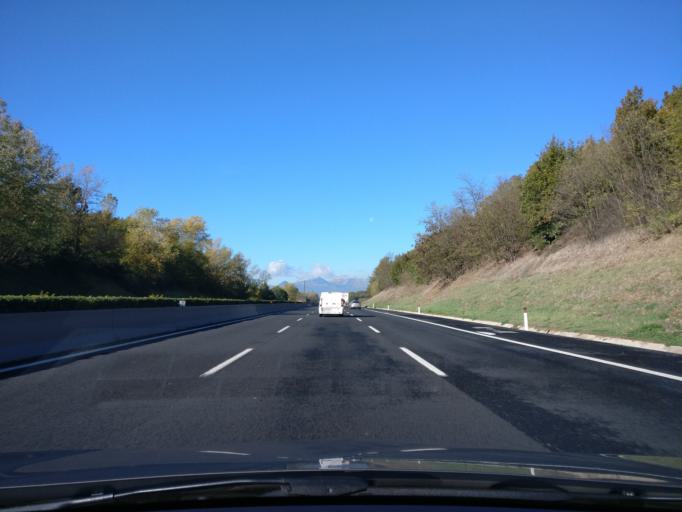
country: IT
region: Latium
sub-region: Provincia di Frosinone
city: Ceprano
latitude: 41.5473
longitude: 13.4738
